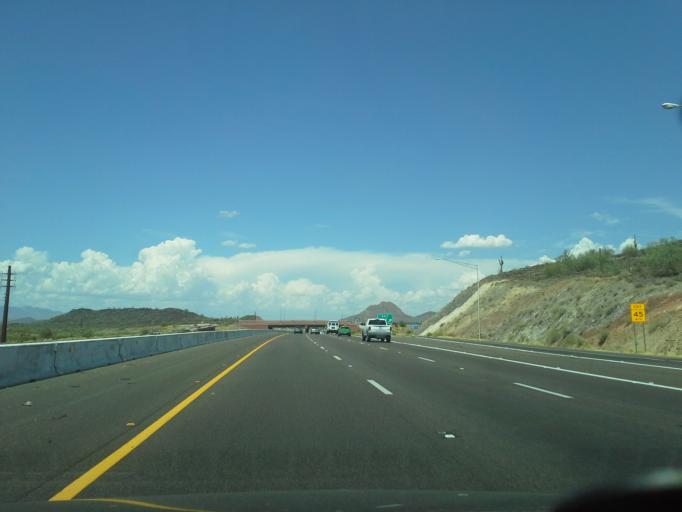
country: US
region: Arizona
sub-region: Maricopa County
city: Anthem
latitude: 33.8364
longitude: -112.1447
